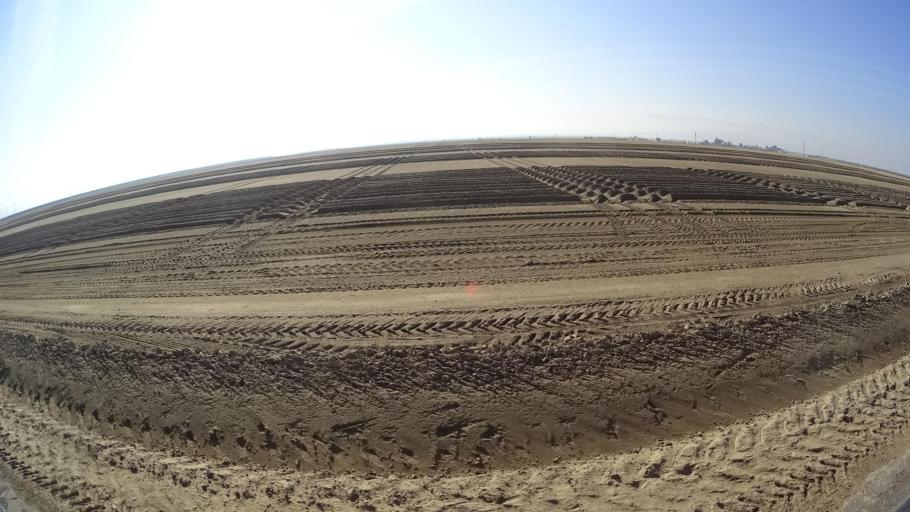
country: US
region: California
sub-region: Kern County
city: Arvin
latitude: 35.1218
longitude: -118.9031
